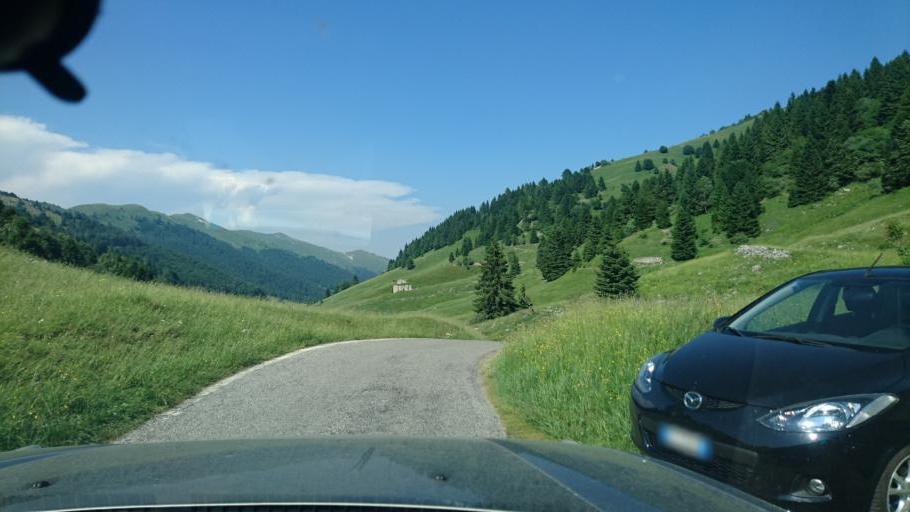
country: IT
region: Veneto
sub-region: Provincia di Treviso
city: Crespano del Grappa
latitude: 45.8830
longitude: 11.8149
